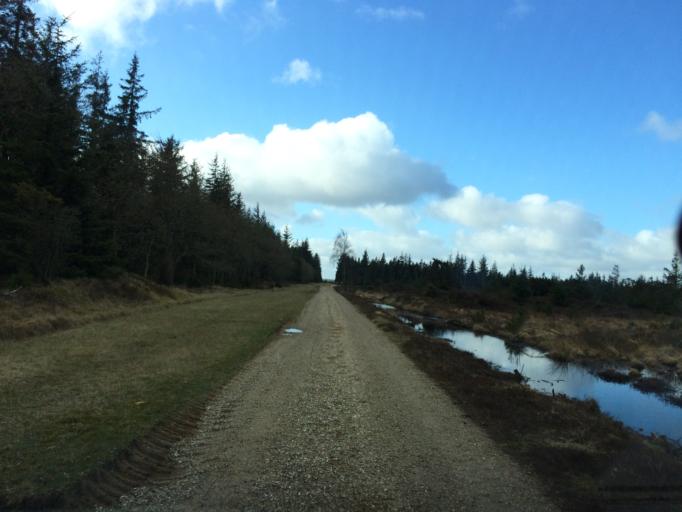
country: DK
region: Central Jutland
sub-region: Holstebro Kommune
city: Ulfborg
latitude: 56.2545
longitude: 8.4463
